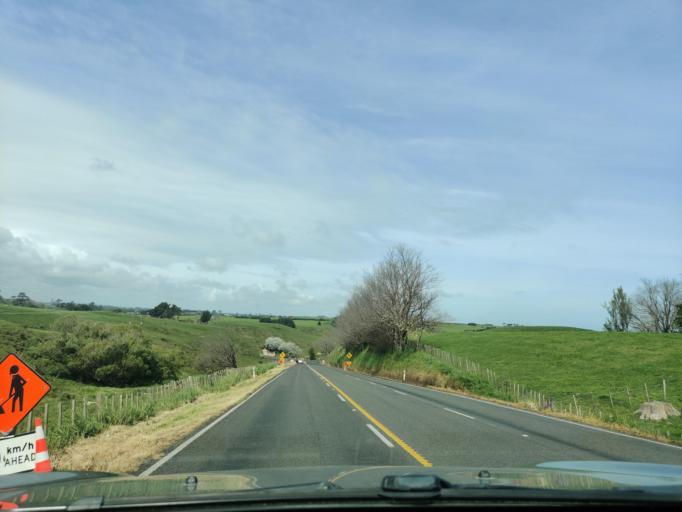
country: NZ
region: Taranaki
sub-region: South Taranaki District
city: Hawera
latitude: -39.6169
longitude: 174.3394
